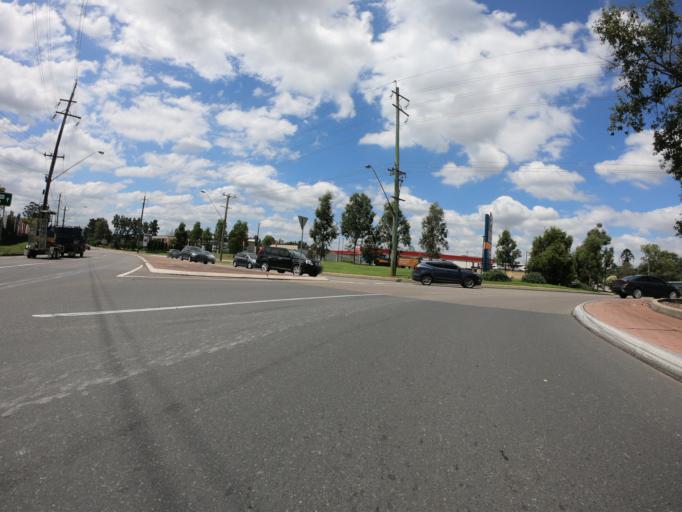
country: AU
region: New South Wales
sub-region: Penrith Municipality
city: Penrith
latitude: -33.7430
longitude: 150.6920
